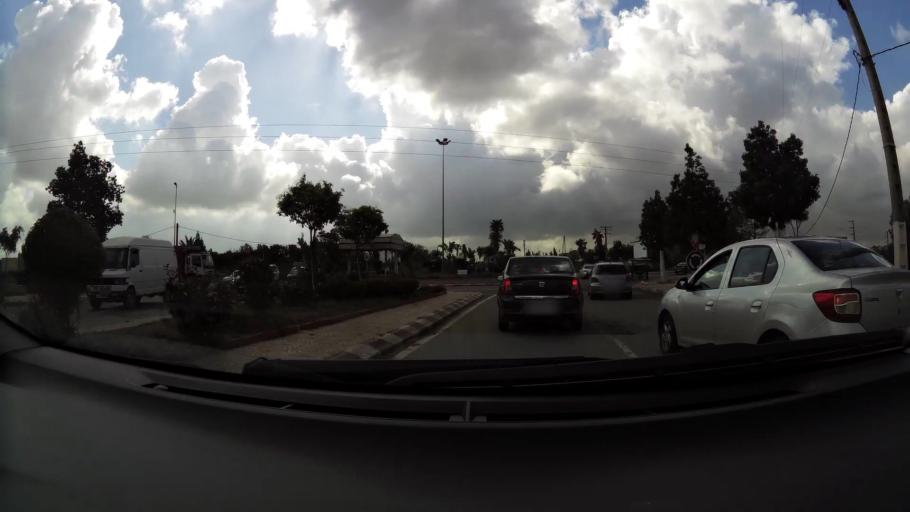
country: MA
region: Grand Casablanca
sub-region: Mediouna
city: Tit Mellil
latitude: 33.5583
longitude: -7.4867
